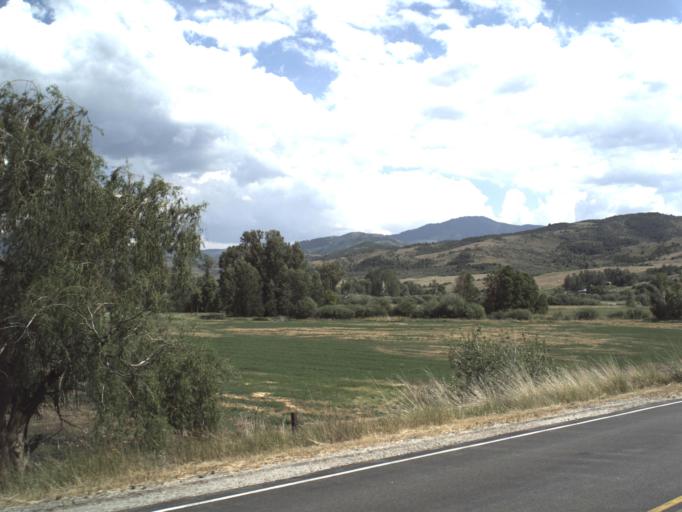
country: US
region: Utah
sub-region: Weber County
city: Wolf Creek
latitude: 41.2544
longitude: -111.7613
